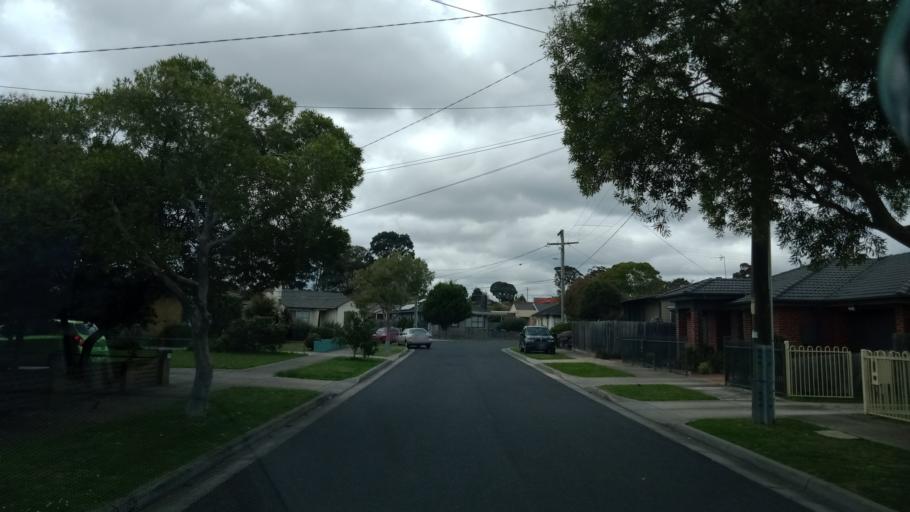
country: AU
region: Victoria
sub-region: Casey
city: Doveton
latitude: -37.9924
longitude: 145.2317
